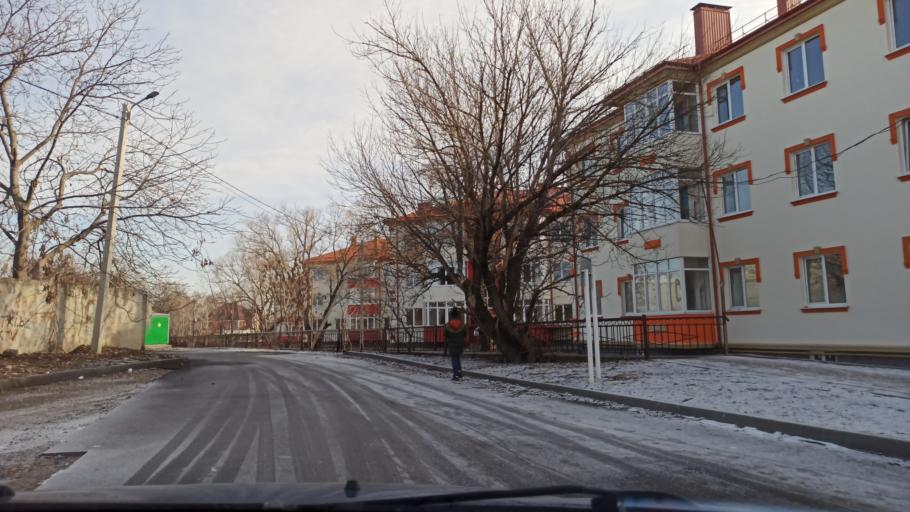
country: RU
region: Stavropol'skiy
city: Yessentukskaya
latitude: 44.0360
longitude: 42.8727
